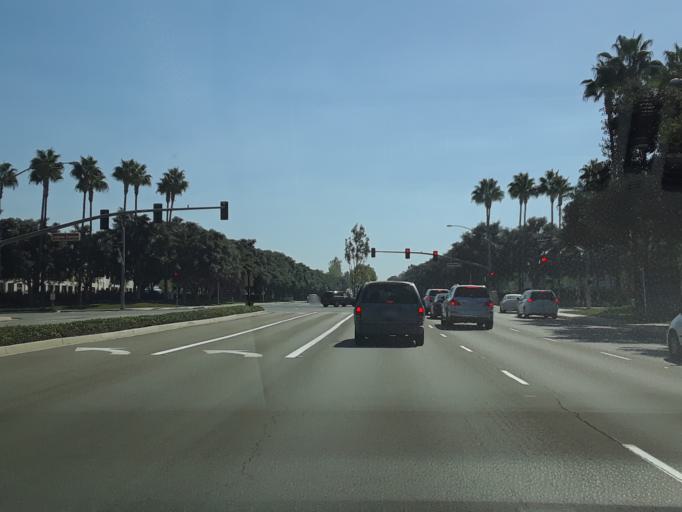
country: US
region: California
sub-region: Orange County
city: Irvine
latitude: 33.6670
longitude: -117.7608
